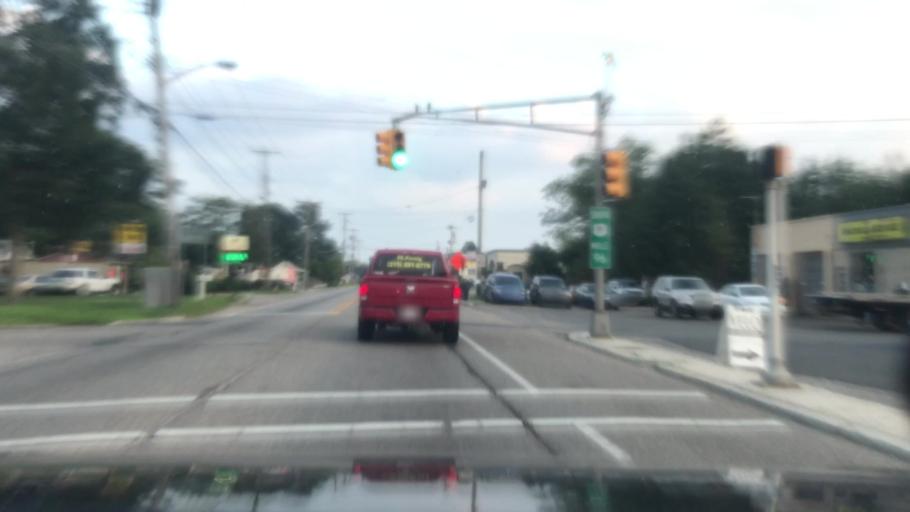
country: US
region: New Jersey
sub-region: Ocean County
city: Pine Lake Park
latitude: 40.0093
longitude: -74.2161
